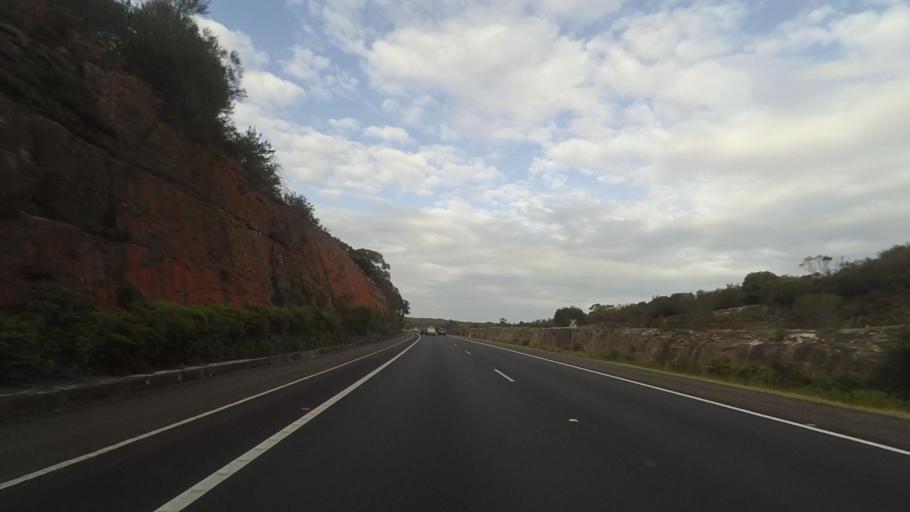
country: AU
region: New South Wales
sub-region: Wollongong
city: Bulli
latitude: -34.2909
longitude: 150.9235
